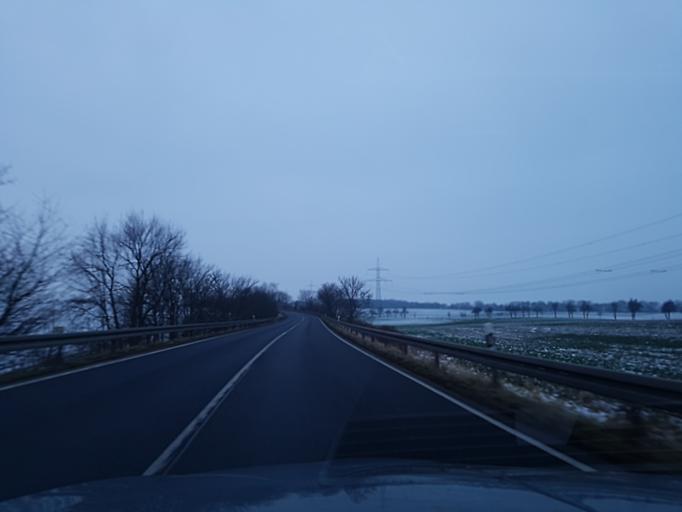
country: DE
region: Saxony
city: Ostrau
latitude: 51.1846
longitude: 13.1441
